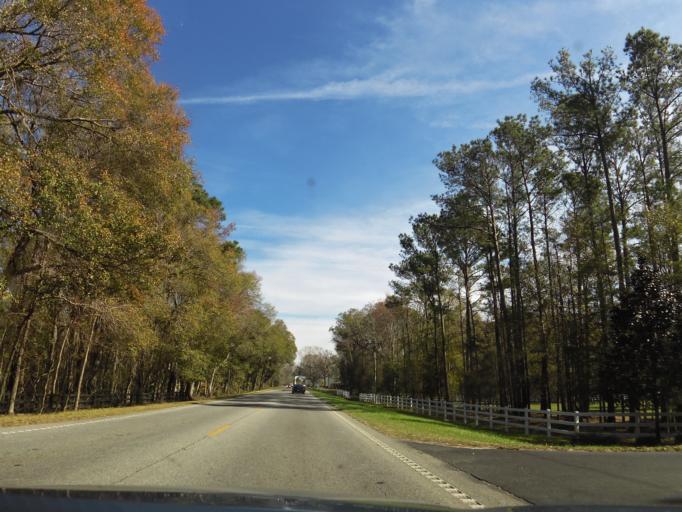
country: US
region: Georgia
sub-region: Glynn County
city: Dock Junction
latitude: 31.2742
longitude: -81.5715
